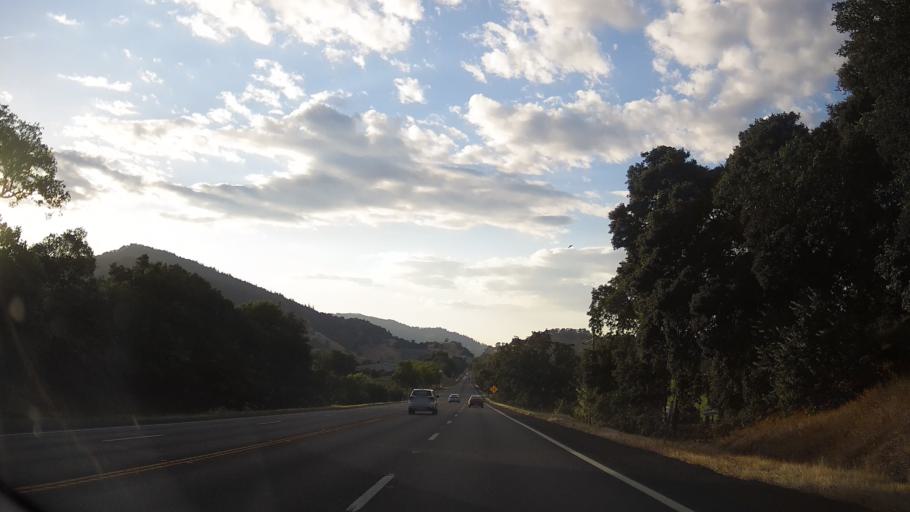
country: US
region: California
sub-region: Mendocino County
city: Talmage
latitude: 39.0114
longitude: -123.1253
